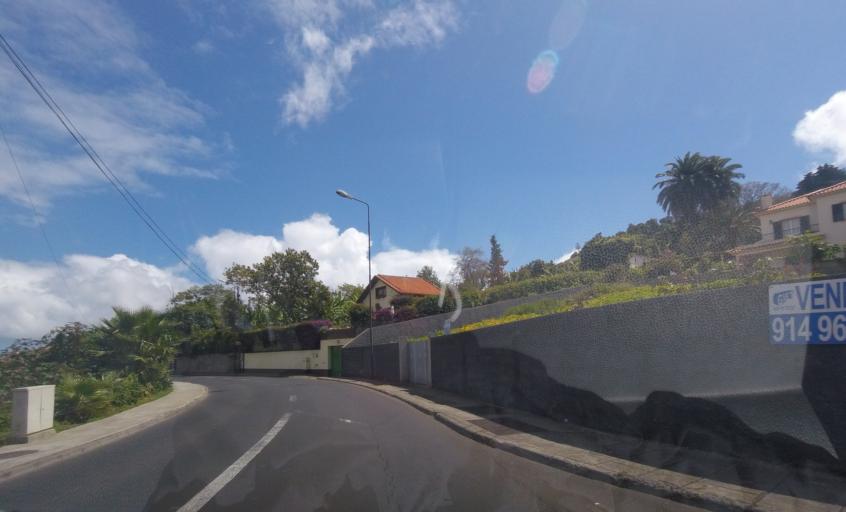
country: PT
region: Madeira
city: Camara de Lobos
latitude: 32.6545
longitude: -16.9363
